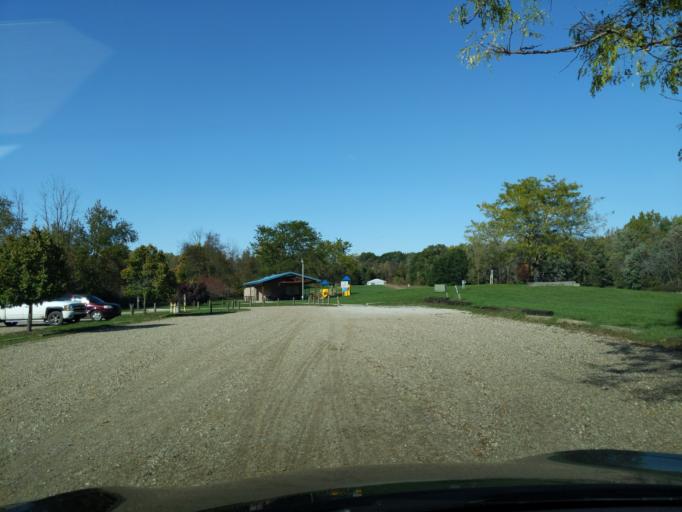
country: US
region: Michigan
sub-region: Eaton County
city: Potterville
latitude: 42.6434
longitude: -84.7607
